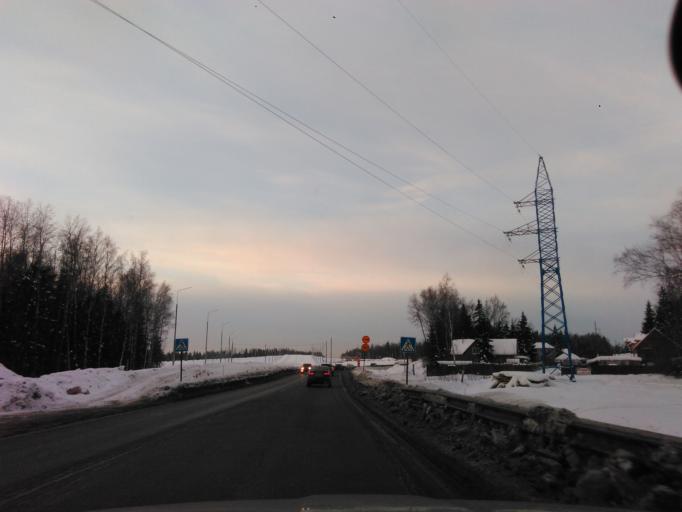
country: RU
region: Moskovskaya
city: Povarovo
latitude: 56.0115
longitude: 37.0279
